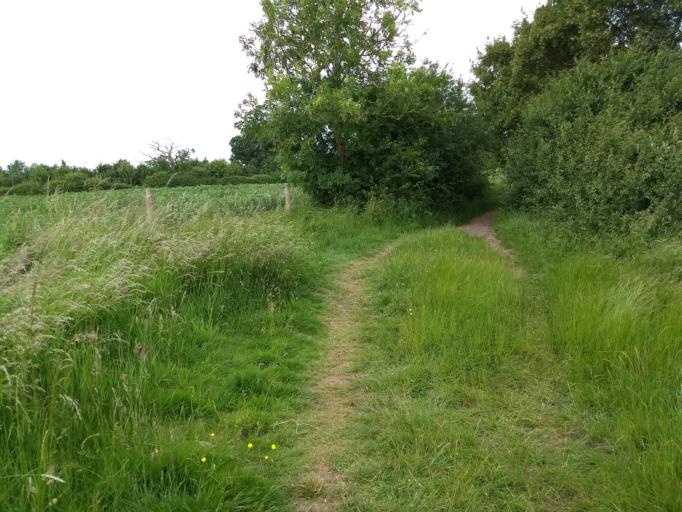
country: GB
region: England
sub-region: Milton Keynes
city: Shenley Church End
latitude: 52.0058
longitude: -0.8120
